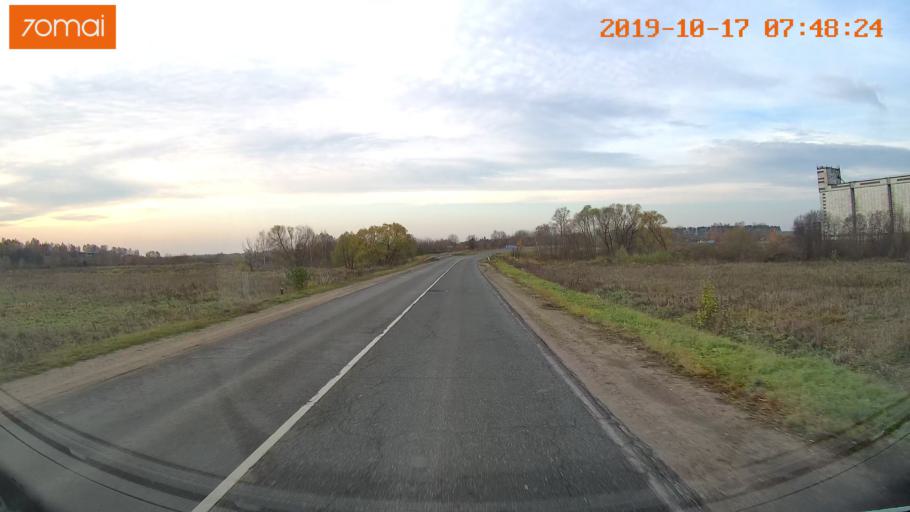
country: RU
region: Vladimir
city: Yur'yev-Pol'skiy
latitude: 56.4801
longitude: 39.6757
